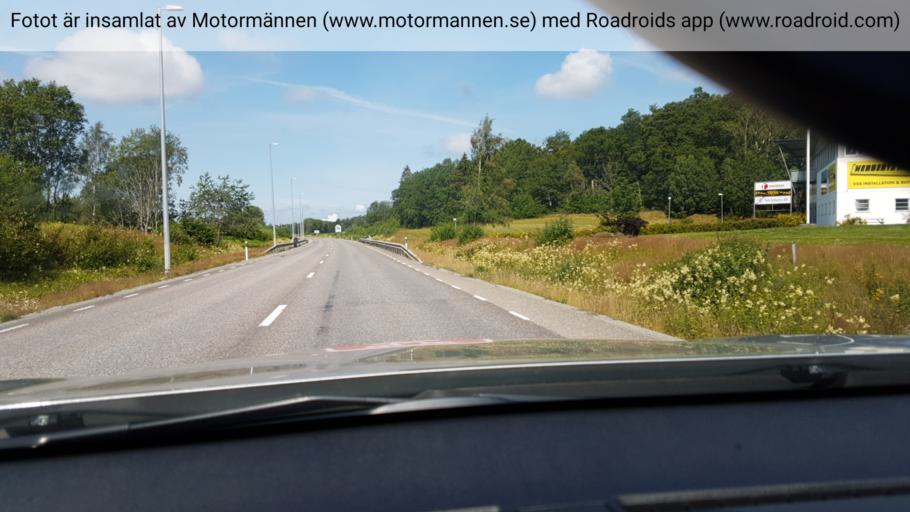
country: SE
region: Vaestra Goetaland
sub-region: Stenungsunds Kommun
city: Stenungsund
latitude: 58.0651
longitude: 11.8667
